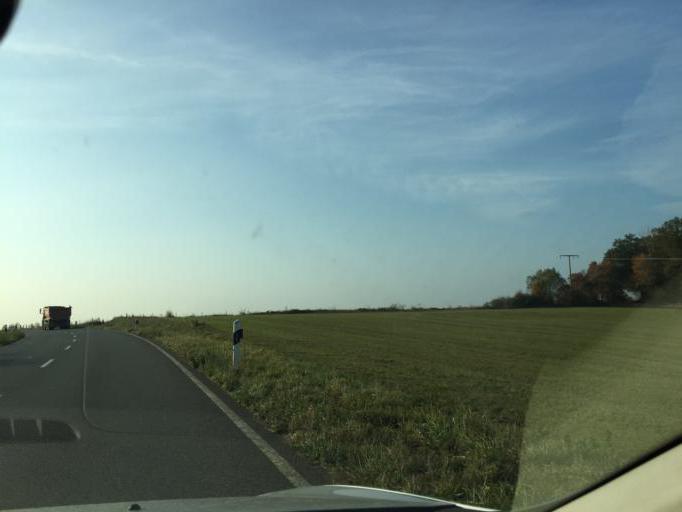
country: LU
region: Luxembourg
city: Aspelt
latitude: 49.5504
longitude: 6.2307
